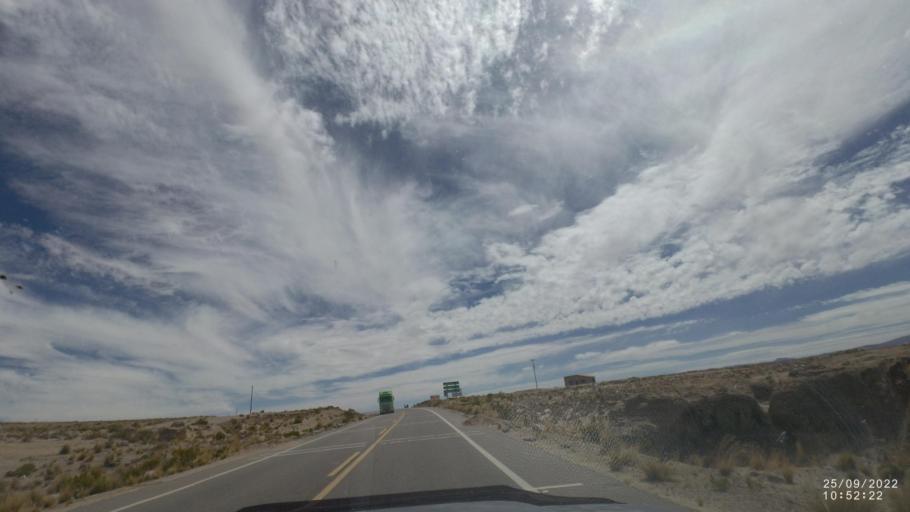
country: BO
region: Oruro
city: Challapata
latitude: -19.5494
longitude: -66.8531
